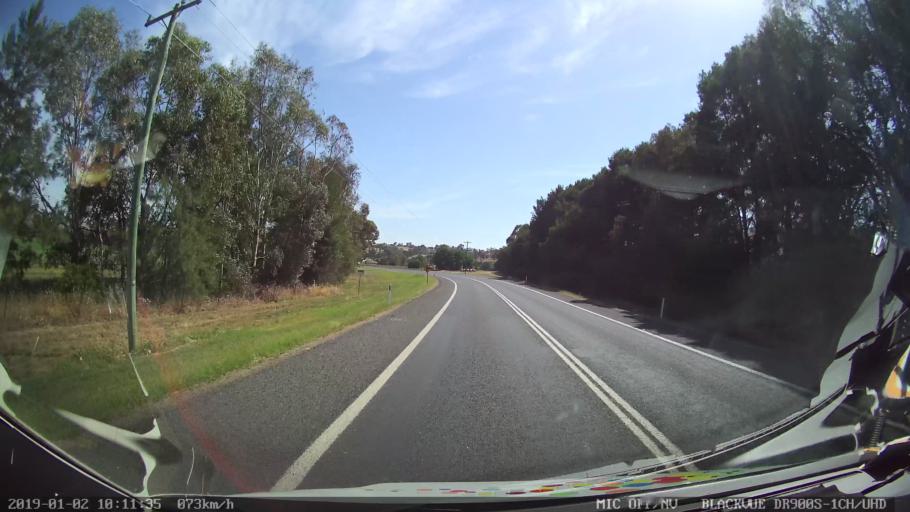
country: AU
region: New South Wales
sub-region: Gundagai
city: Gundagai
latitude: -35.0916
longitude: 148.0935
